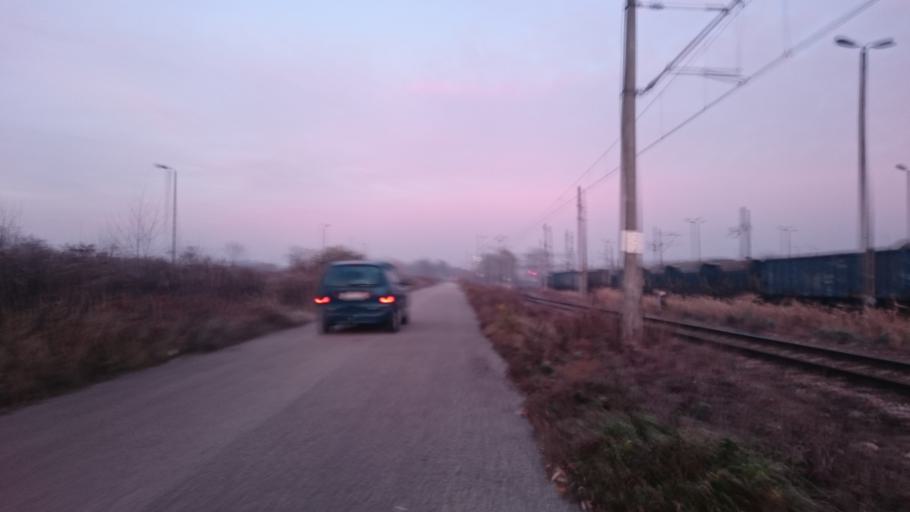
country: PL
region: Lesser Poland Voivodeship
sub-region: Powiat wielicki
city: Czarnochowice
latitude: 50.0271
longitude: 20.0079
